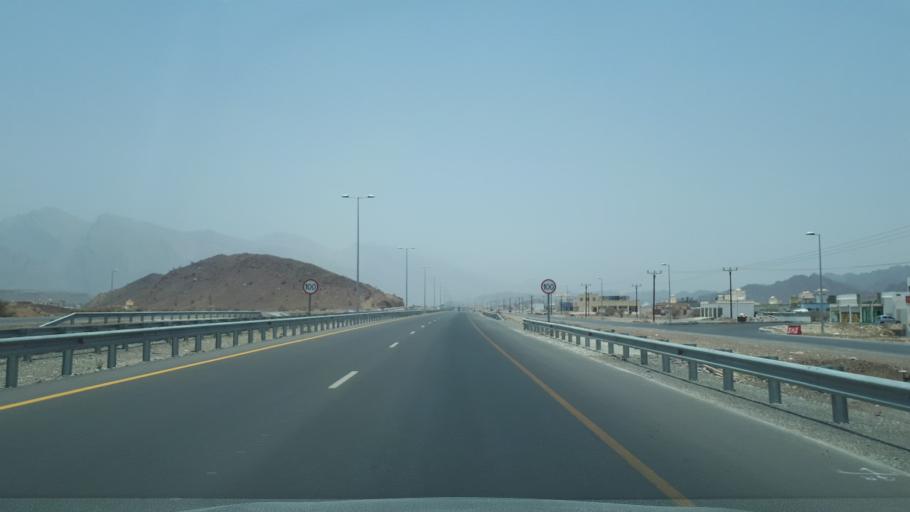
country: OM
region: Al Batinah
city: Rustaq
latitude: 23.4281
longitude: 57.3800
